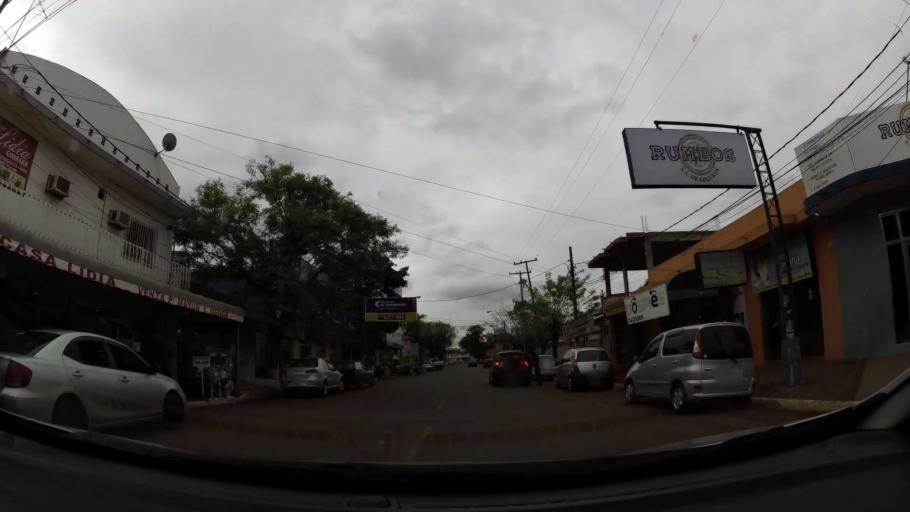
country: PY
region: Alto Parana
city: Ciudad del Este
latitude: -25.3999
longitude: -54.6406
